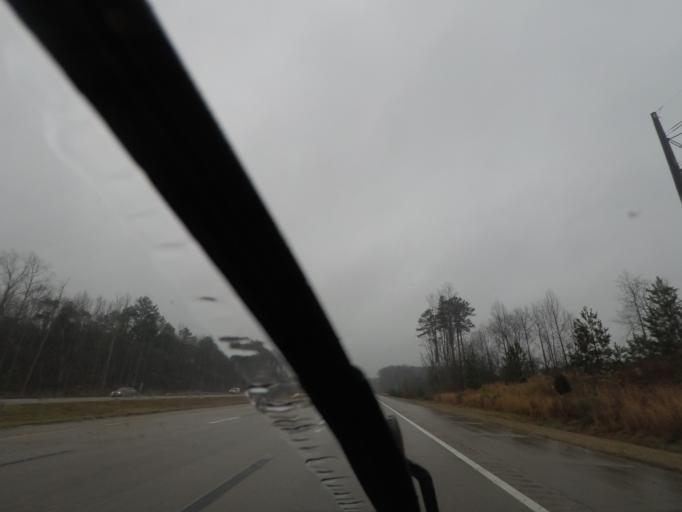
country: US
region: North Carolina
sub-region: Wake County
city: Green Level
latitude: 35.7657
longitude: -78.8881
